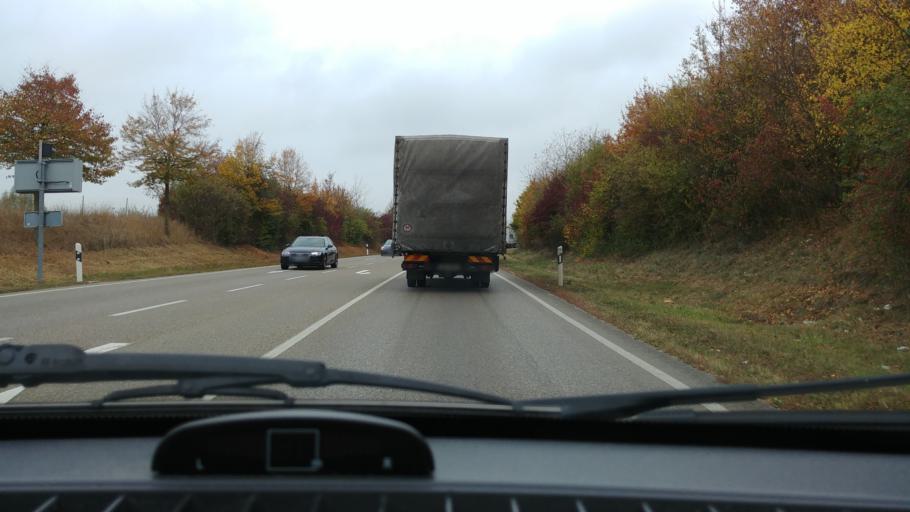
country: DE
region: Baden-Wuerttemberg
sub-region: Regierungsbezirk Stuttgart
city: Aalen
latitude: 48.8396
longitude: 10.0656
